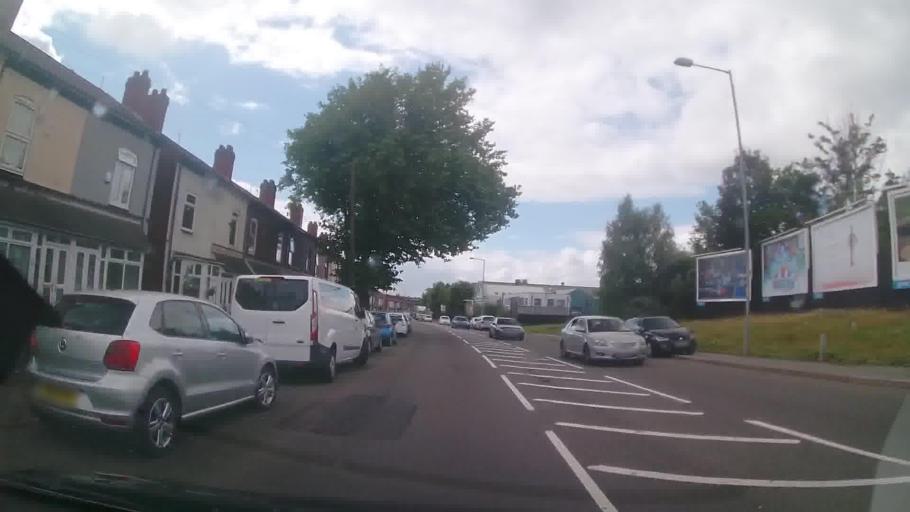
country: GB
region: England
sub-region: Walsall
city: Walsall
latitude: 52.5757
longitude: -2.0080
